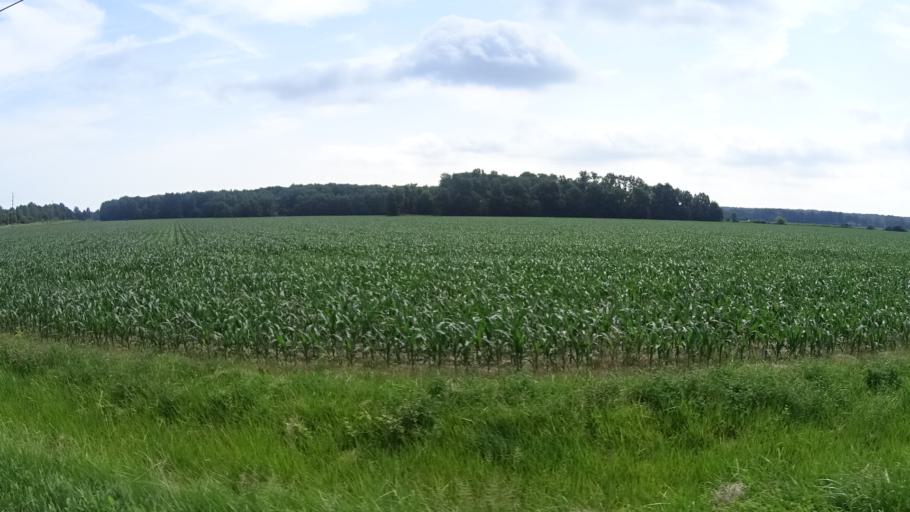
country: US
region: Ohio
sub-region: Lorain County
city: Vermilion
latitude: 41.3934
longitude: -82.4062
